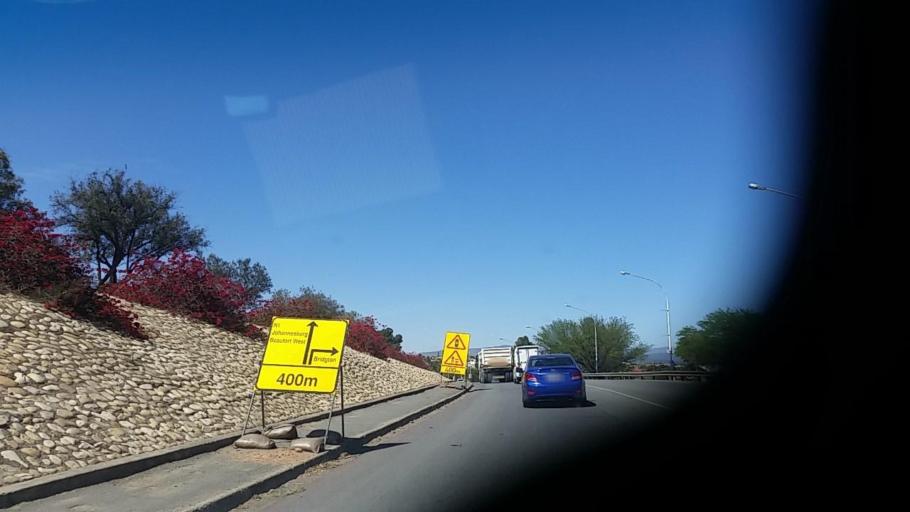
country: ZA
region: Western Cape
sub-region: Eden District Municipality
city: Oudtshoorn
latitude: -33.5948
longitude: 22.2174
